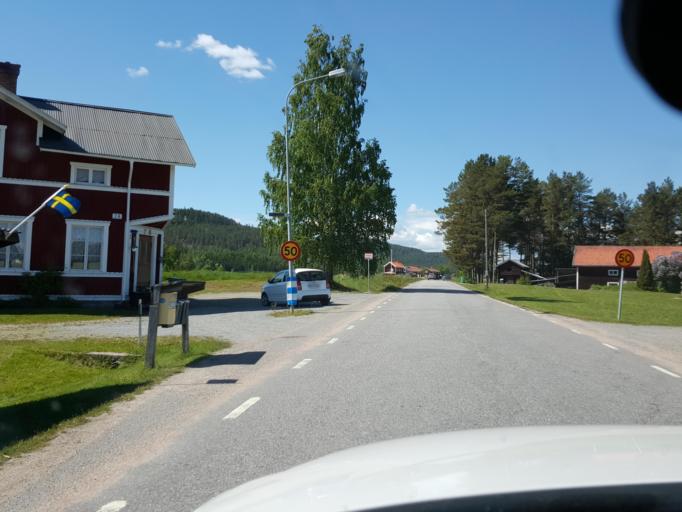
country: SE
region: Gaevleborg
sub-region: Ljusdals Kommun
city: Jaervsoe
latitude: 61.7122
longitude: 16.2992
